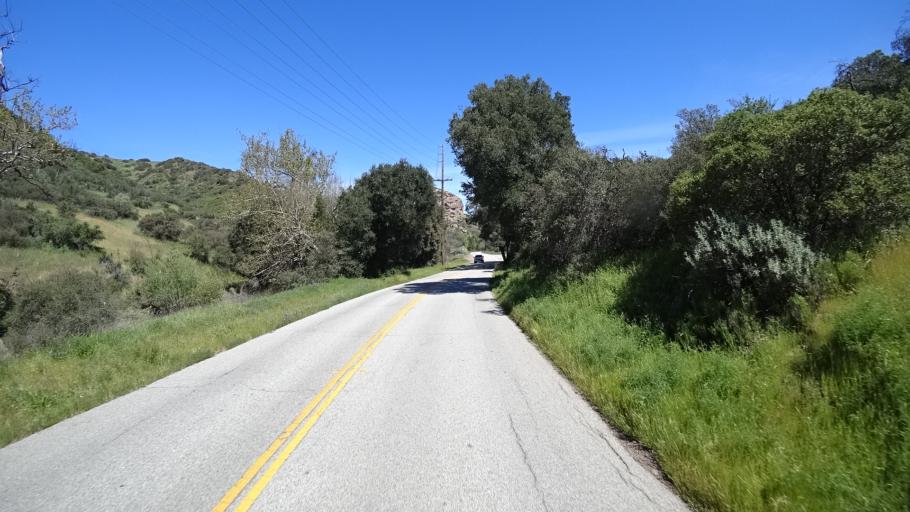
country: US
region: California
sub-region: Ventura County
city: Thousand Oaks
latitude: 34.1281
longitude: -118.8557
